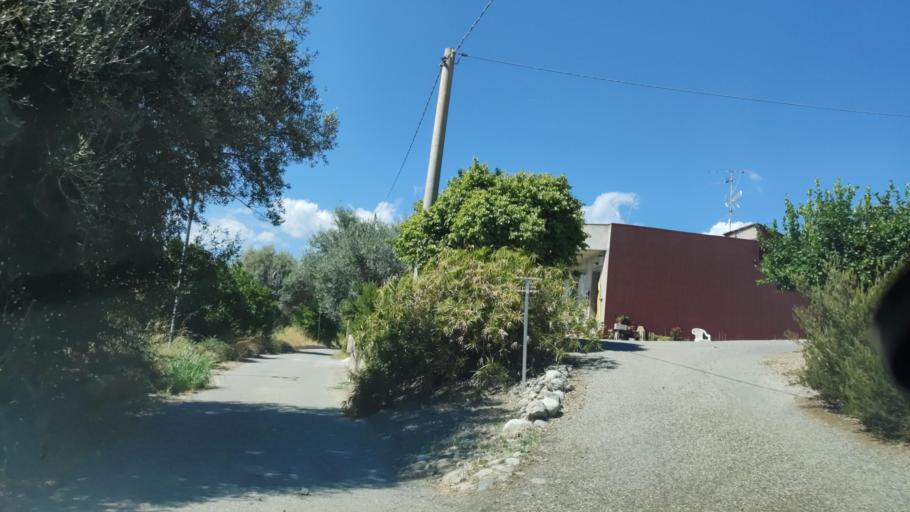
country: IT
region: Calabria
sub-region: Provincia di Reggio Calabria
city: Monasterace Marina
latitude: 38.4388
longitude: 16.5561
